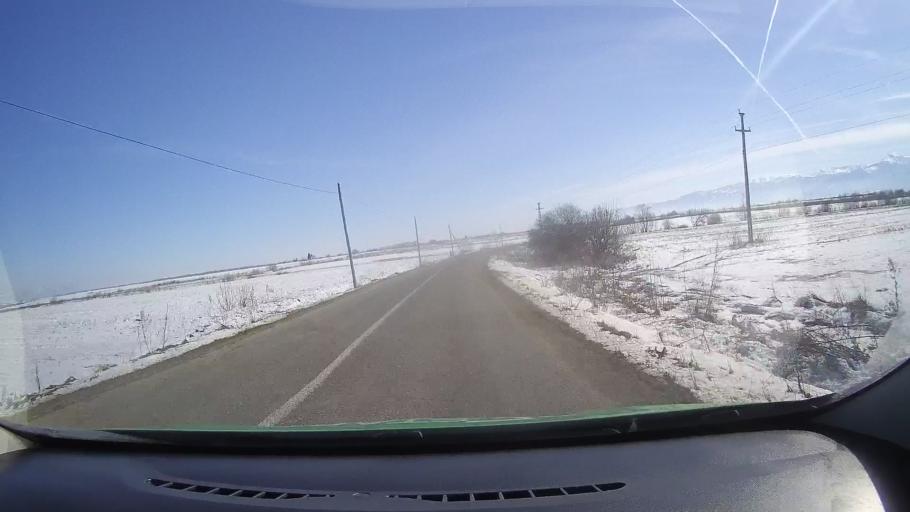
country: RO
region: Brasov
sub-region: Comuna Sambata de Sus
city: Sambata de Sus
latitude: 45.7628
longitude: 24.8009
